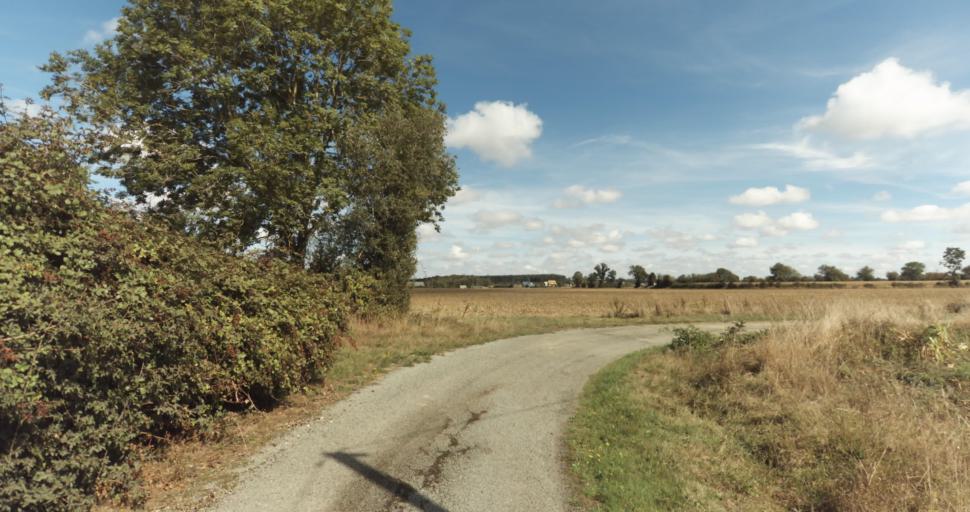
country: FR
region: Lower Normandy
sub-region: Departement du Calvados
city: Orbec
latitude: 48.9630
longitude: 0.4006
